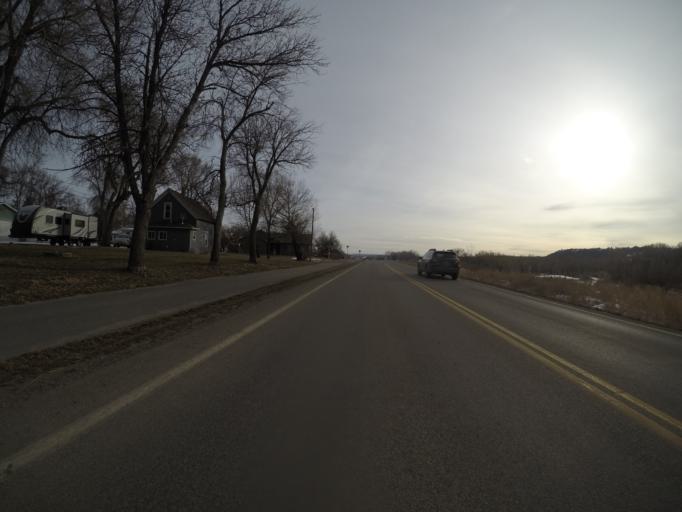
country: US
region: Montana
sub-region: Stillwater County
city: Columbus
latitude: 45.6393
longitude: -109.2621
